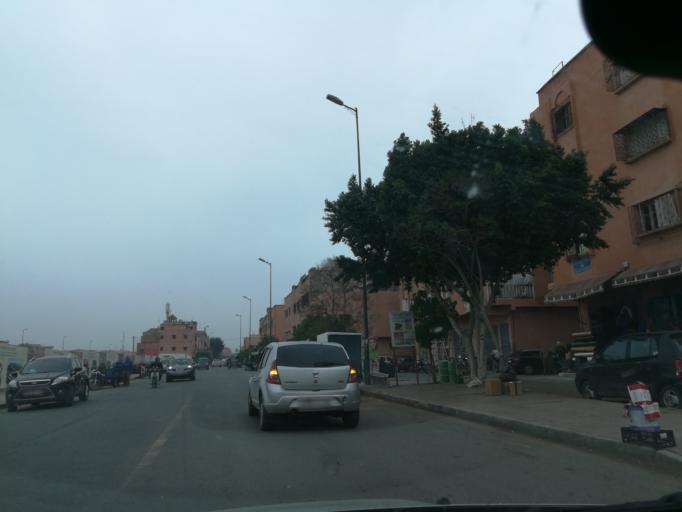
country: MA
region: Marrakech-Tensift-Al Haouz
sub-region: Marrakech
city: Marrakesh
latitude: 31.6552
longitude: -7.9902
